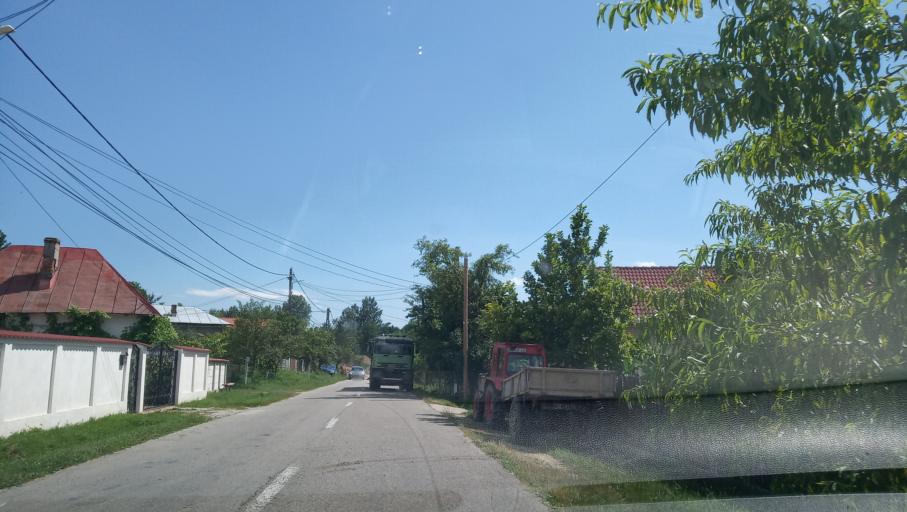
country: RO
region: Valcea
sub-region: Comuna Barbatesti
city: Bodesti
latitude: 45.1417
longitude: 24.1454
